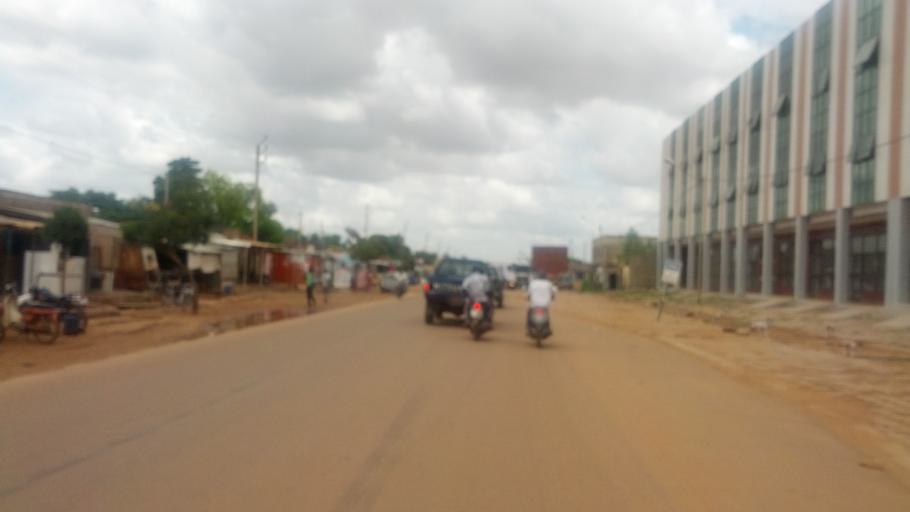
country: BF
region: Centre
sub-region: Kadiogo Province
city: Ouagadougou
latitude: 12.3505
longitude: -1.5008
